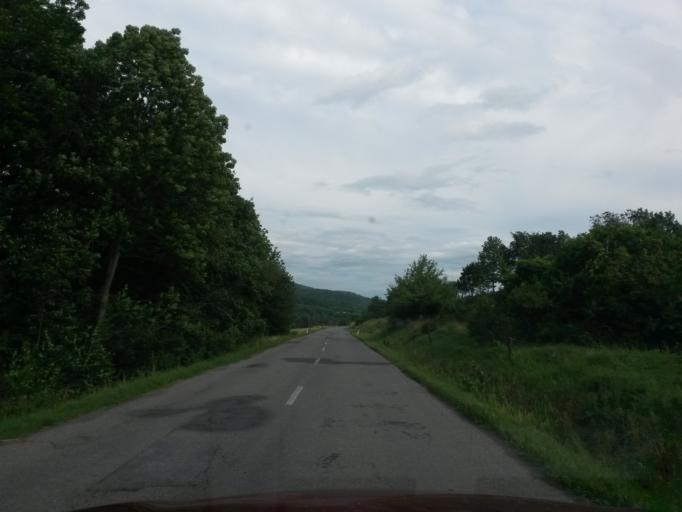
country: SK
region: Banskobystricky
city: Detva
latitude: 48.4329
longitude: 19.3490
